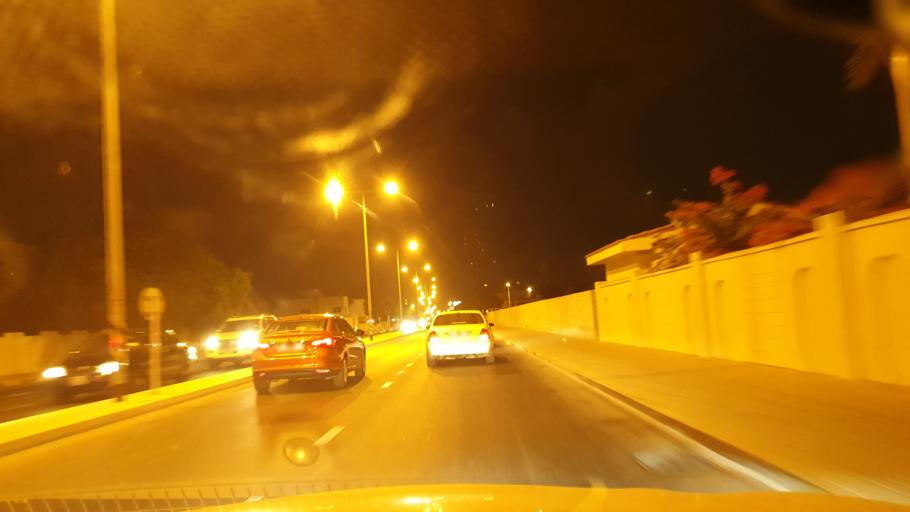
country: BH
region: Manama
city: Jidd Hafs
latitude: 26.2008
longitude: 50.4848
